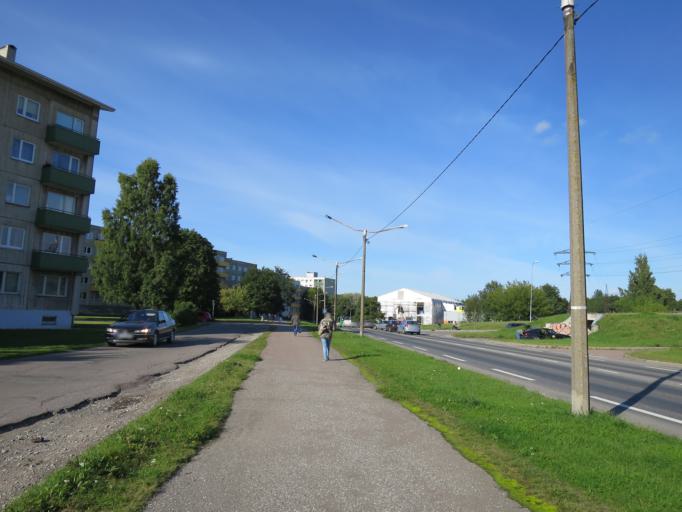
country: EE
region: Harju
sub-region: Tallinna linn
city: Tallinn
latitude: 59.4008
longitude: 24.7059
